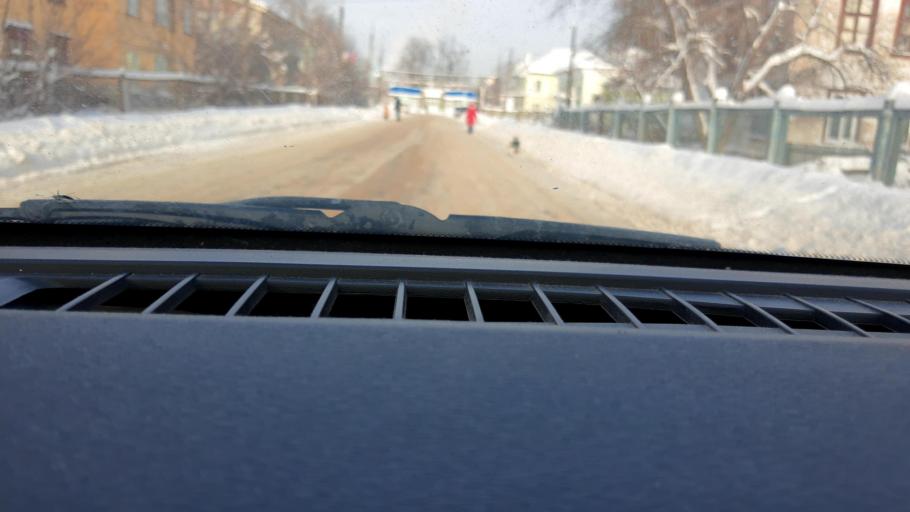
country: RU
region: Nizjnij Novgorod
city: Lukino
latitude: 56.3365
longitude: 43.6179
